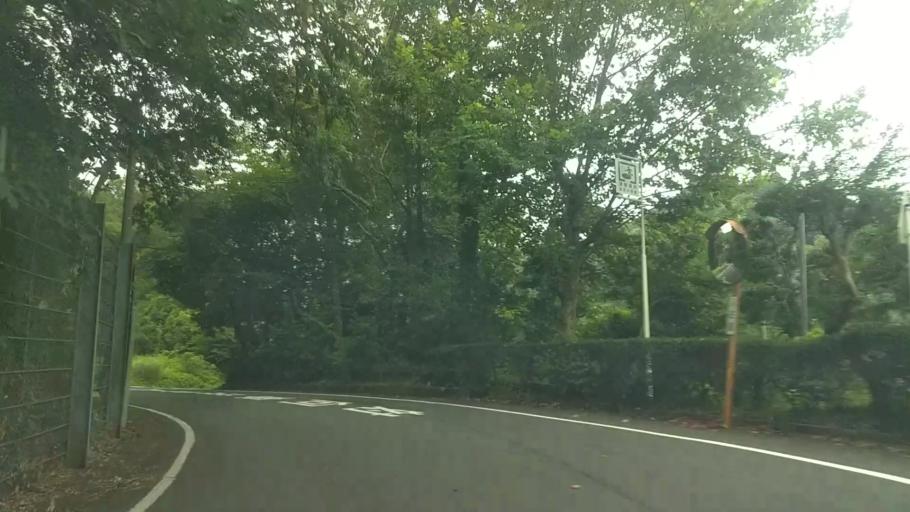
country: JP
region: Chiba
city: Kawaguchi
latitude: 35.2530
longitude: 140.0604
